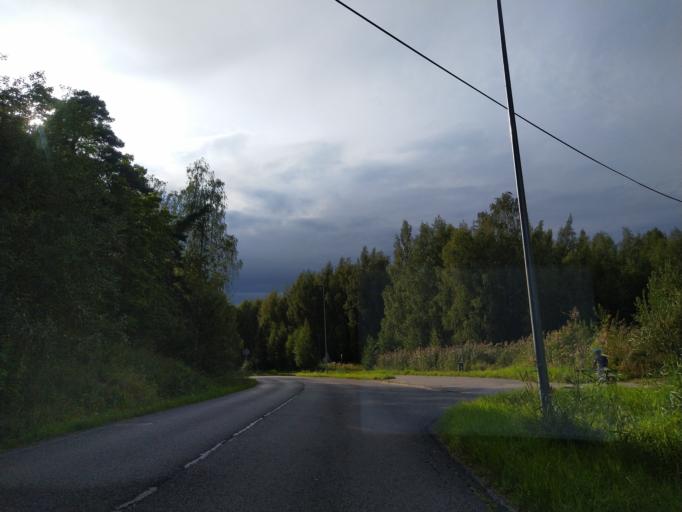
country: FI
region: Varsinais-Suomi
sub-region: Turku
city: Turku
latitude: 60.4295
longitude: 22.2212
